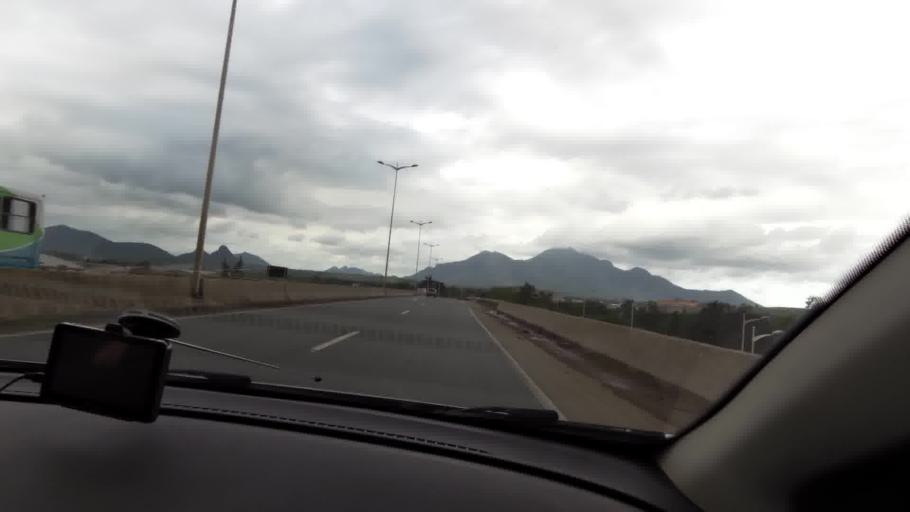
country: BR
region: Espirito Santo
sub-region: Vitoria
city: Vitoria
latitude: -20.2287
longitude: -40.3661
